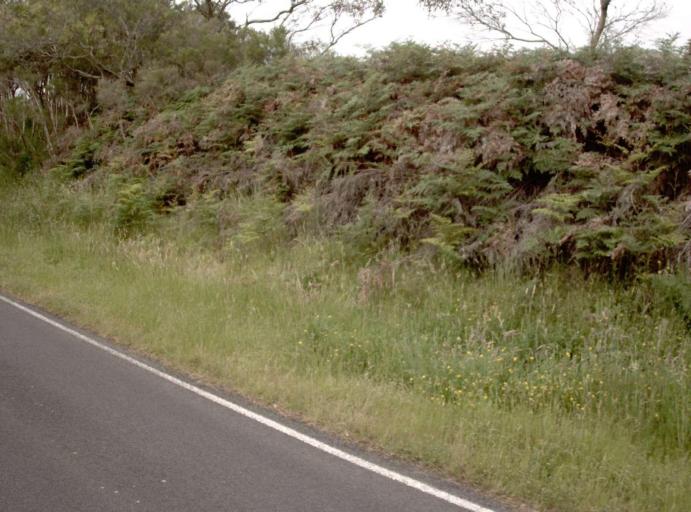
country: AU
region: Victoria
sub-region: Bass Coast
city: North Wonthaggi
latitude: -38.5400
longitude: 145.6980
